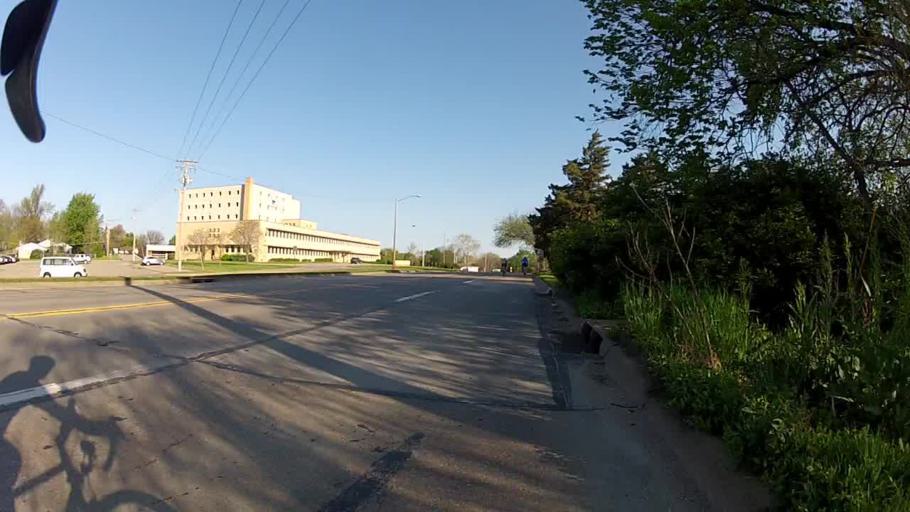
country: US
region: Kansas
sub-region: Riley County
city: Manhattan
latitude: 39.1882
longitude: -96.5984
